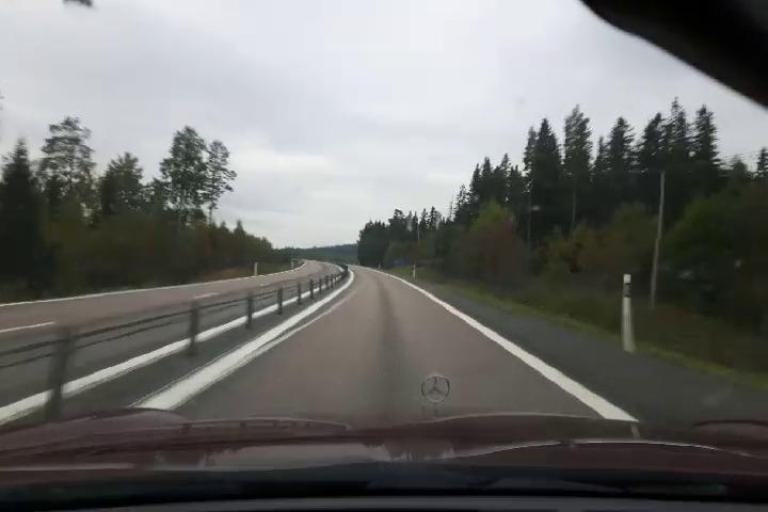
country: SE
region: Vaesternorrland
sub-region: Kramfors Kommun
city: Nordingra
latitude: 62.9081
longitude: 18.0927
